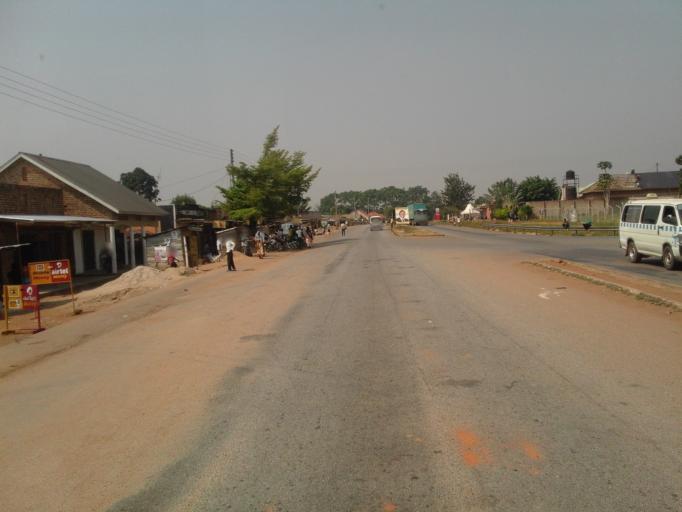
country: UG
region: Eastern Region
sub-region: Iganga District
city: Iganga
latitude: 0.6286
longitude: 33.5184
